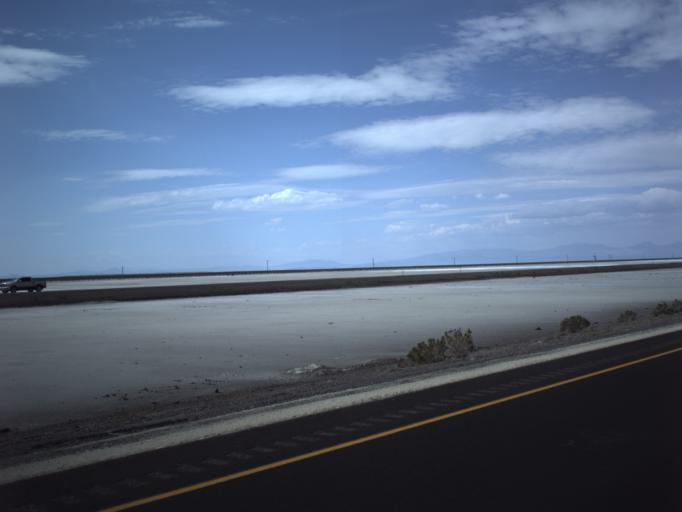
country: US
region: Utah
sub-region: Tooele County
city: Wendover
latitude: 40.7323
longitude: -113.5216
